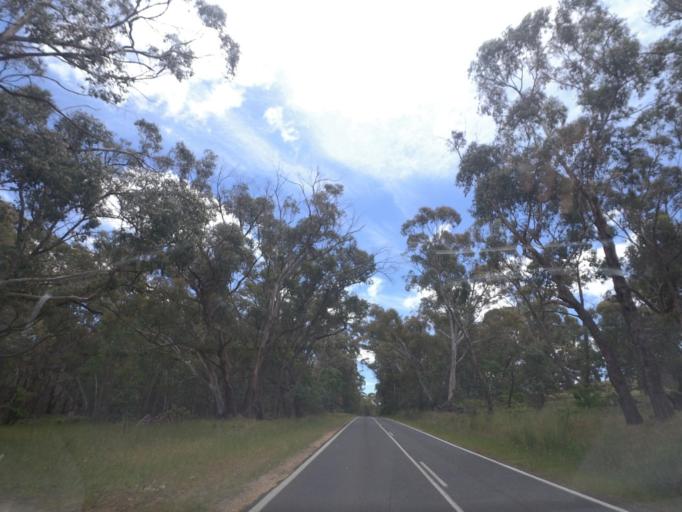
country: AU
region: Victoria
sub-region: Mount Alexander
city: Castlemaine
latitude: -37.3273
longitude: 144.1648
